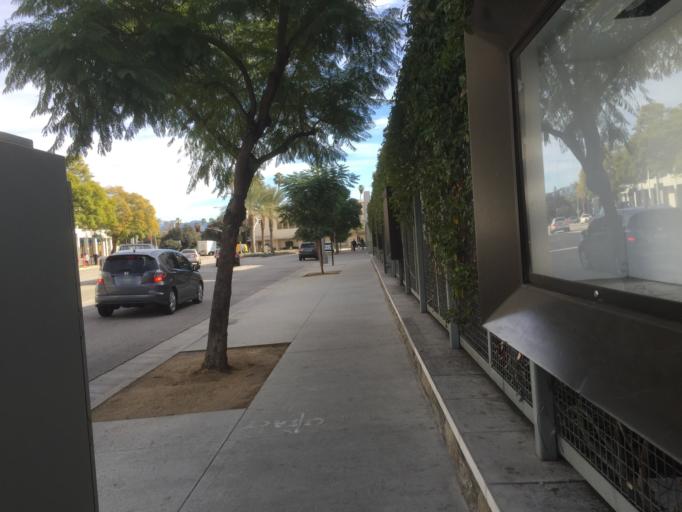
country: US
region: California
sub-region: Los Angeles County
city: Pasadena
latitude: 34.1404
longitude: -118.1337
